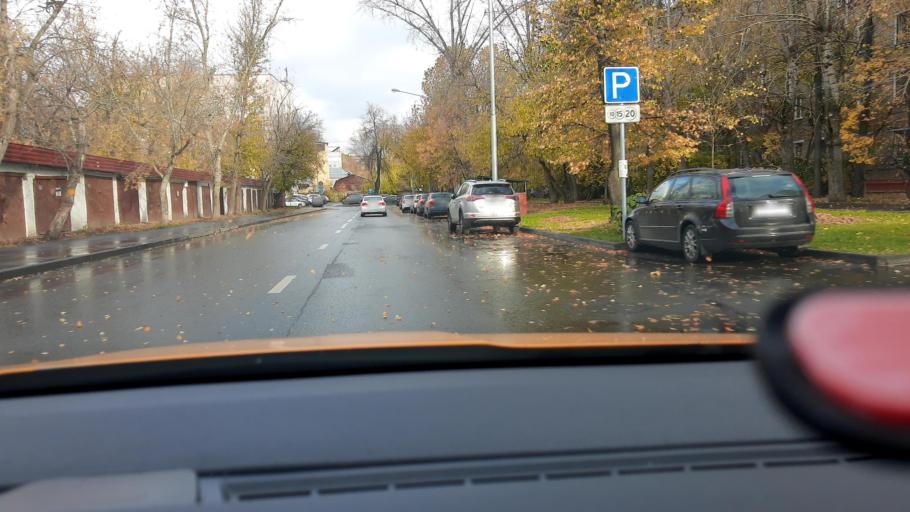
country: RU
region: Moscow
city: Lefortovo
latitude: 55.7757
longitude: 37.7320
